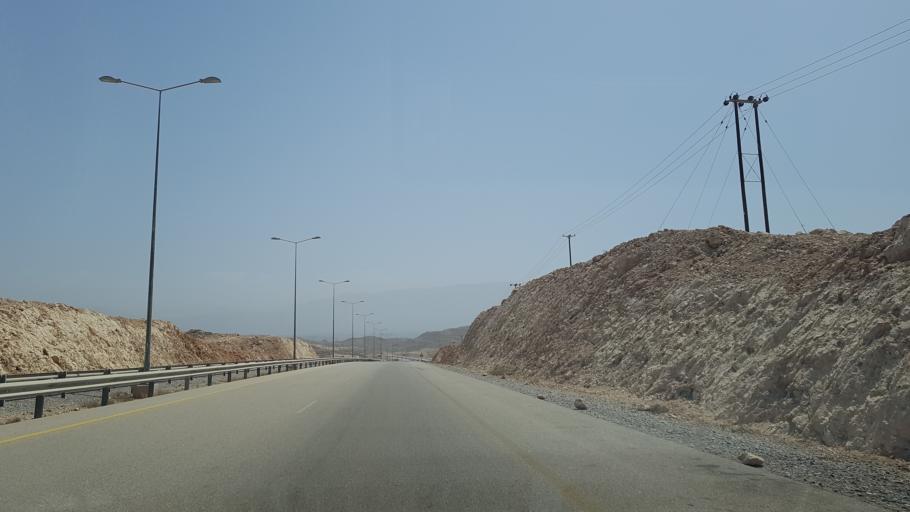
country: OM
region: Muhafazat Masqat
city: Muscat
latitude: 23.1715
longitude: 58.9777
